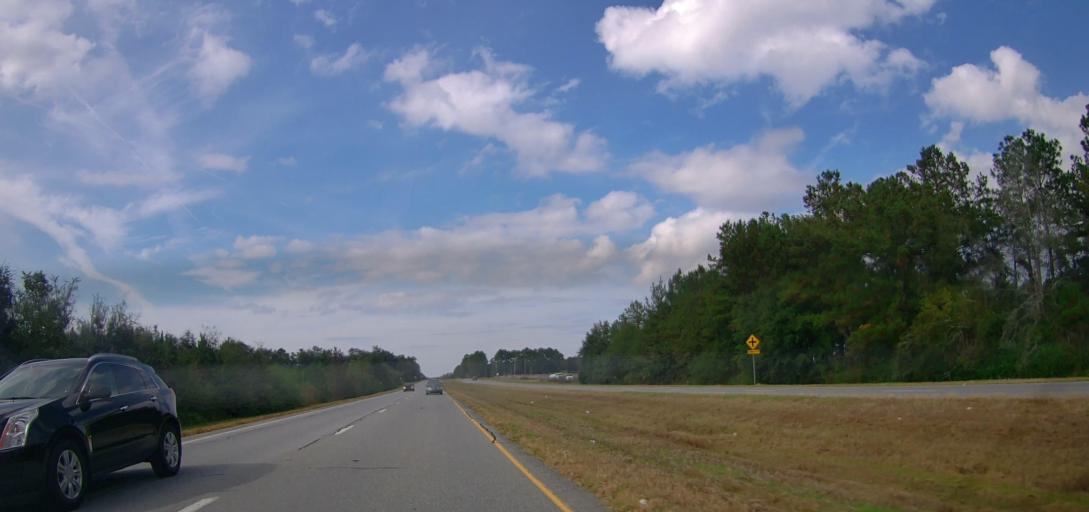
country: US
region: Georgia
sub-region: Mitchell County
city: Camilla
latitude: 31.1977
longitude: -84.1673
